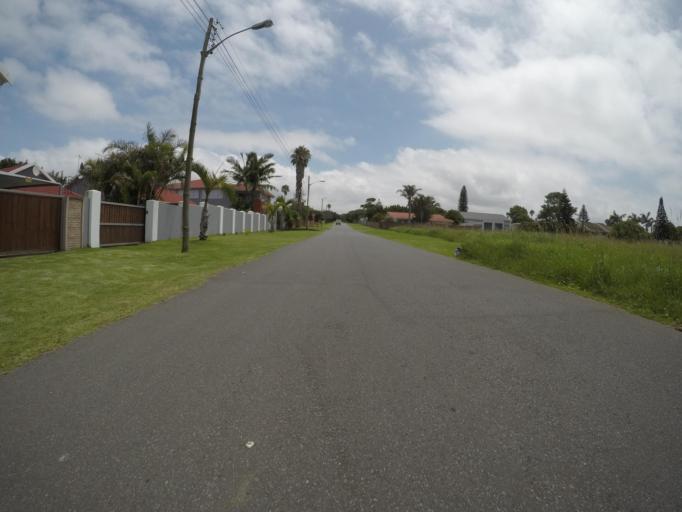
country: ZA
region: Eastern Cape
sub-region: Buffalo City Metropolitan Municipality
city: East London
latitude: -32.9448
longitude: 28.0091
